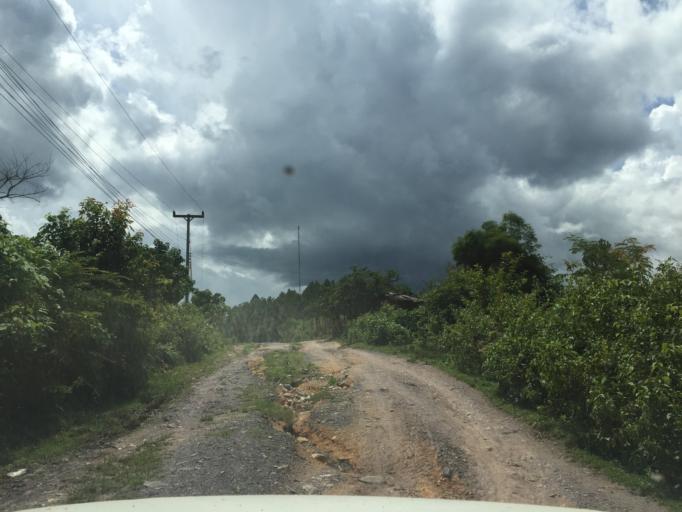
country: LA
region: Xiangkhoang
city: Muang Phonsavan
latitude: 19.3383
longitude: 103.6162
